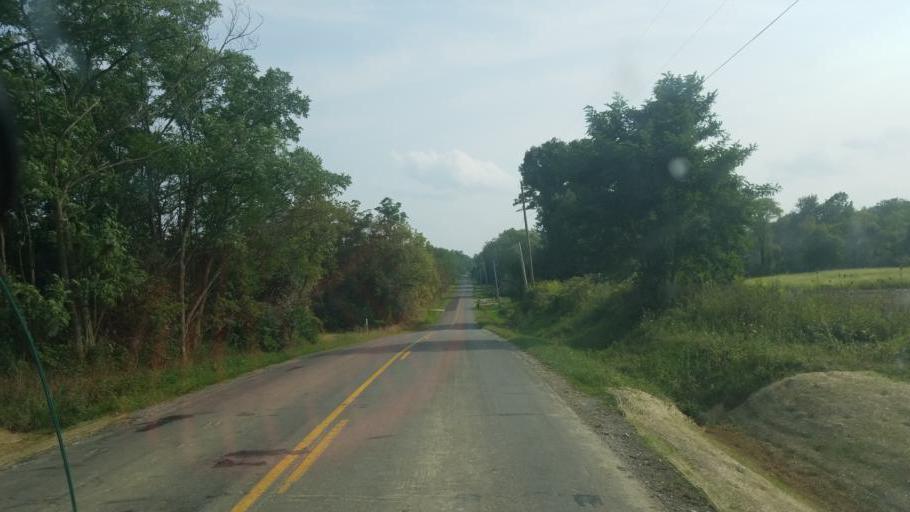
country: US
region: Ohio
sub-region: Medina County
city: Medina
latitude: 41.0909
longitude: -81.8841
